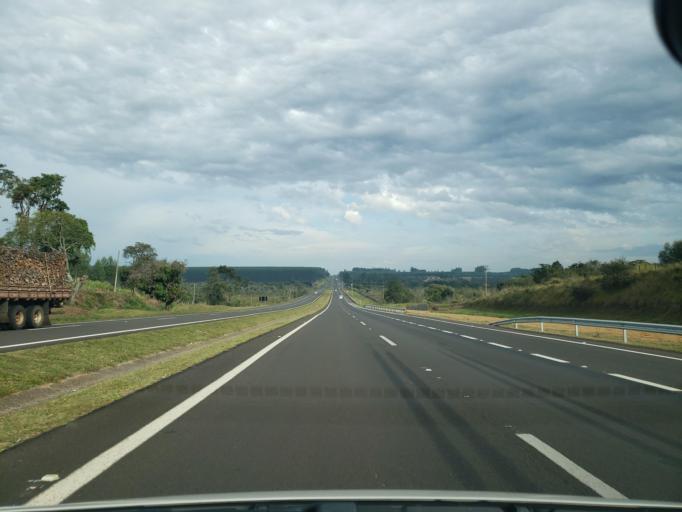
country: BR
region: Sao Paulo
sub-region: Itirapina
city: Itirapina
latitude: -22.2569
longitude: -47.8569
